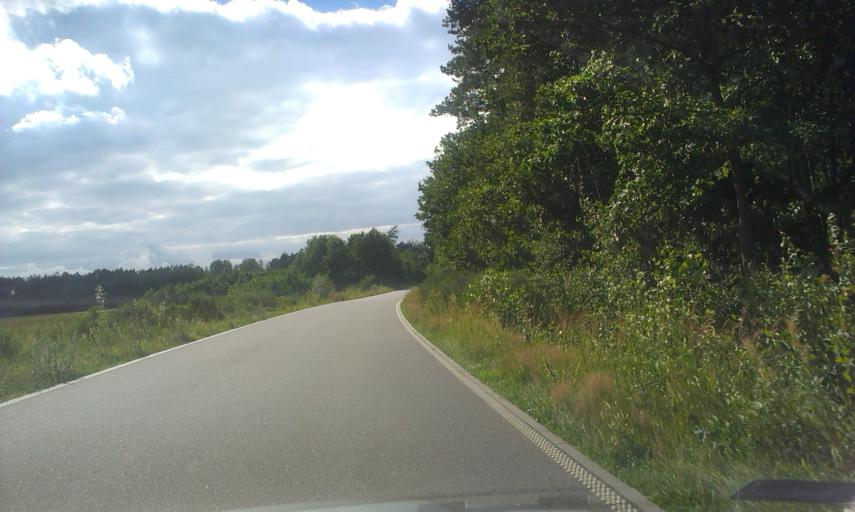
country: PL
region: Masovian Voivodeship
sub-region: Powiat zyrardowski
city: Radziejowice
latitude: 51.9676
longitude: 20.5913
